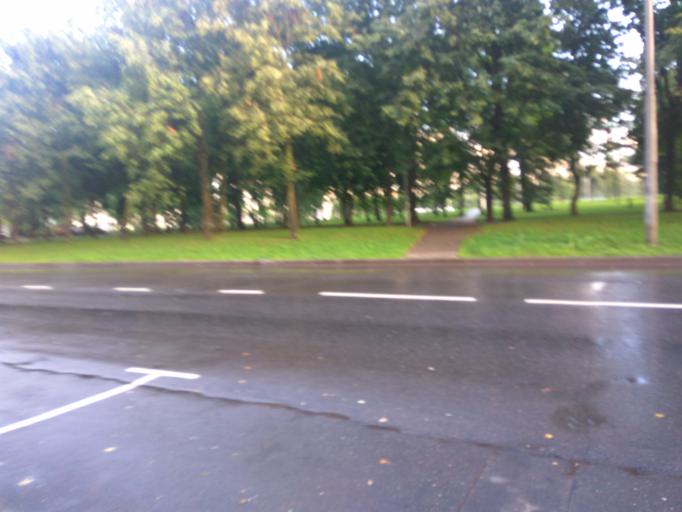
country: RU
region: Moskovskaya
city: Marfino
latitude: 55.7156
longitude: 37.3916
